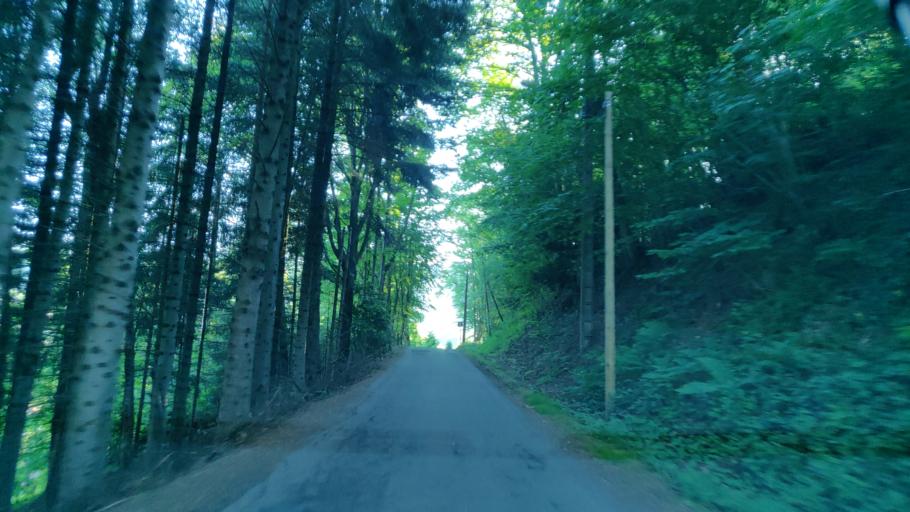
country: FR
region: Lorraine
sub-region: Departement des Vosges
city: Saint-Die-des-Vosges
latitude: 48.2908
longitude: 6.9613
